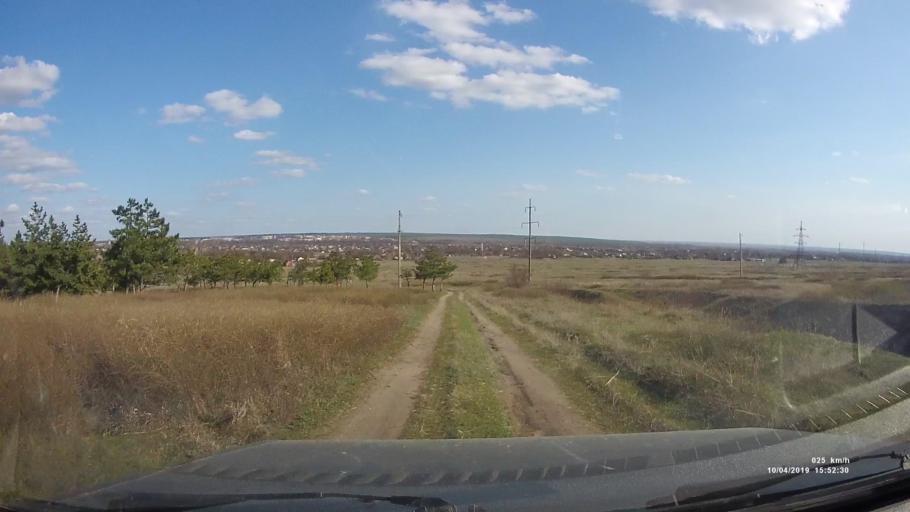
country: RU
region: Rostov
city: Masalovka
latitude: 48.4197
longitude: 40.2567
